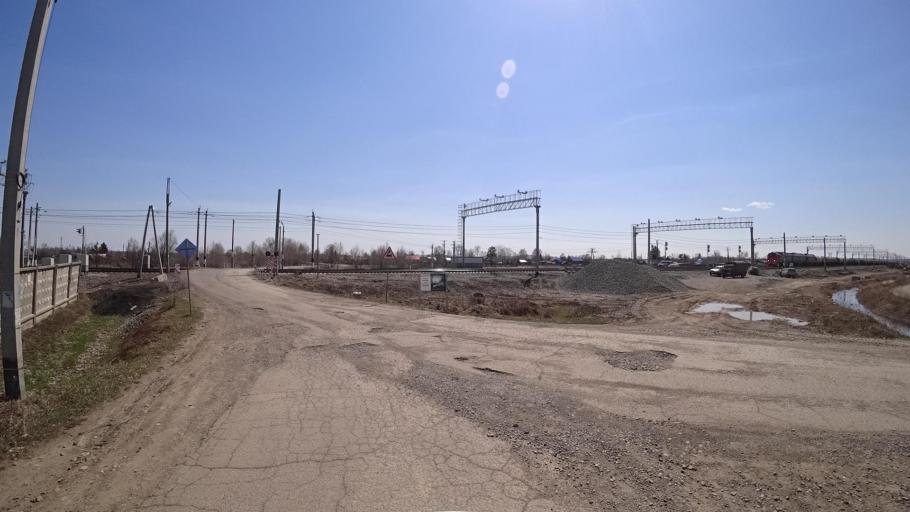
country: RU
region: Khabarovsk Krai
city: Khurba
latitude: 50.4122
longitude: 136.8807
